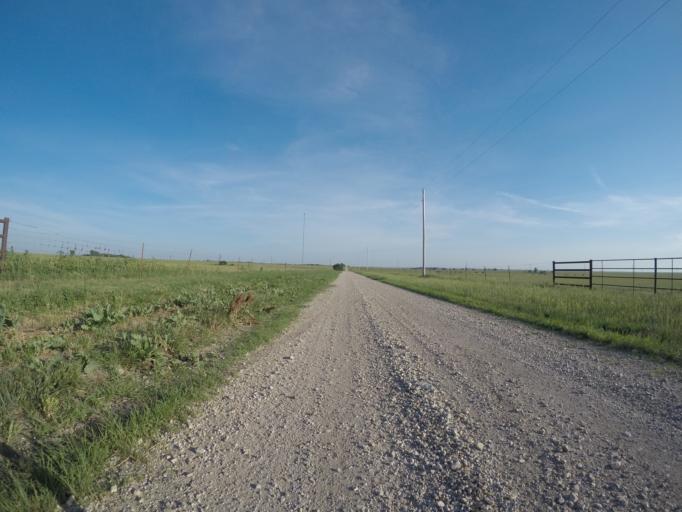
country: US
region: Kansas
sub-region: Riley County
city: Manhattan
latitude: 39.0076
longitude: -96.4920
